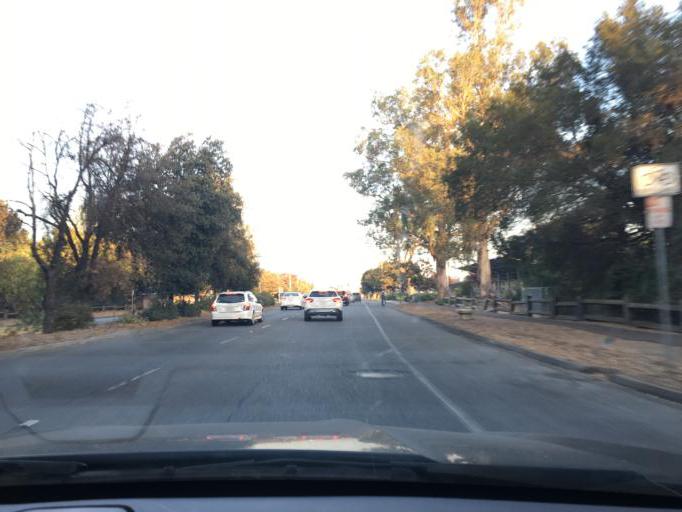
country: US
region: California
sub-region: Santa Clara County
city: Saratoga
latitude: 37.2931
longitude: -122.0041
